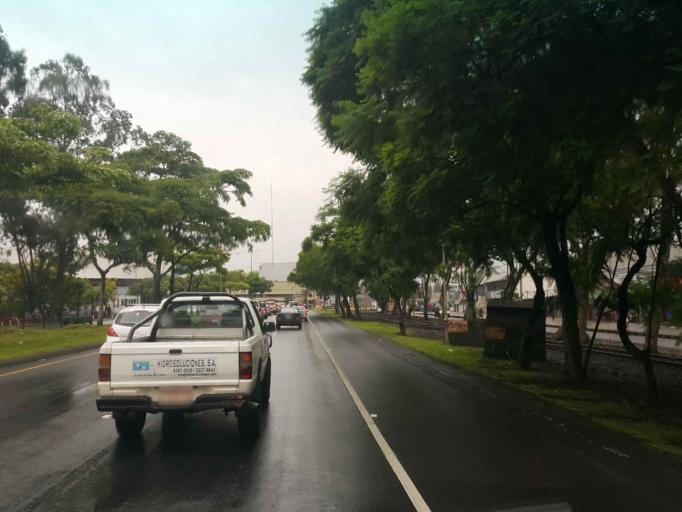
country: CR
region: San Jose
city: San Jose
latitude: 9.9327
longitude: -84.1003
